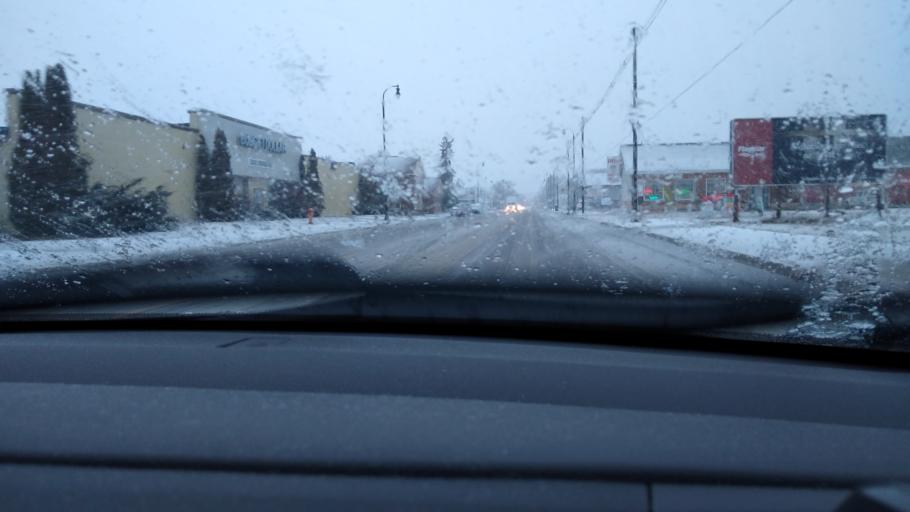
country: US
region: Michigan
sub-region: Delta County
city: Escanaba
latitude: 45.7500
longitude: -87.0719
